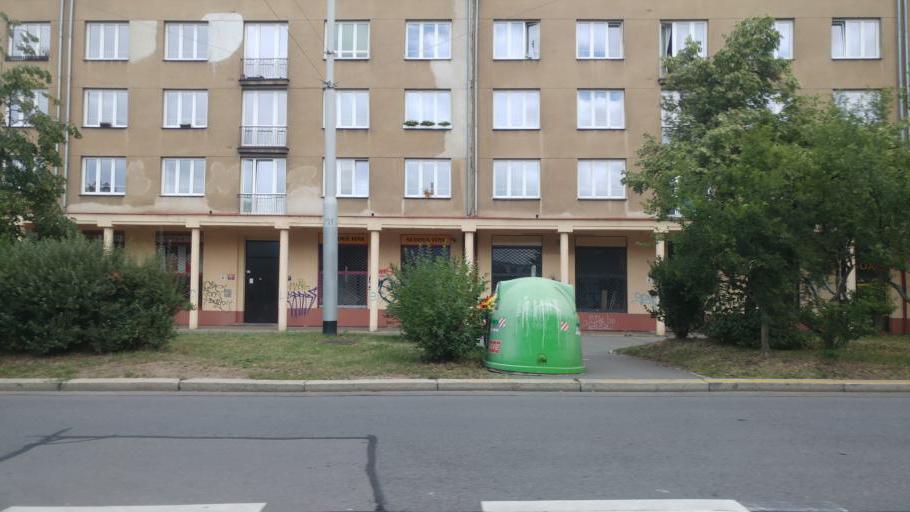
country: CZ
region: Praha
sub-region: Praha 8
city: Liben
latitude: 50.0672
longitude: 14.4951
